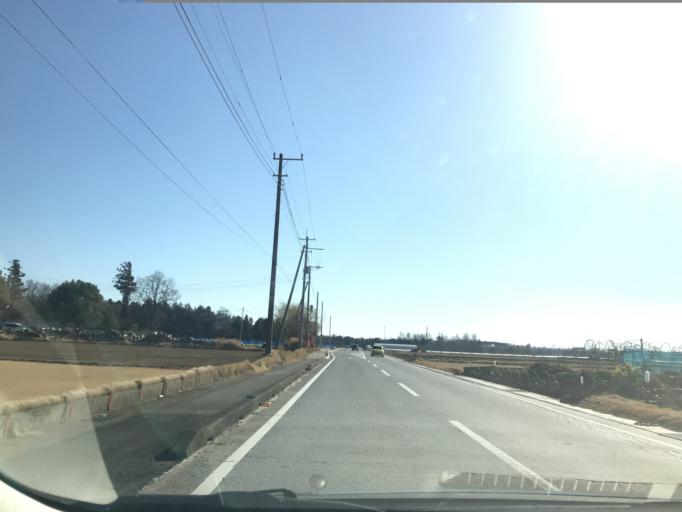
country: JP
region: Ibaraki
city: Tsukuba
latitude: 36.1184
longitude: 140.0602
